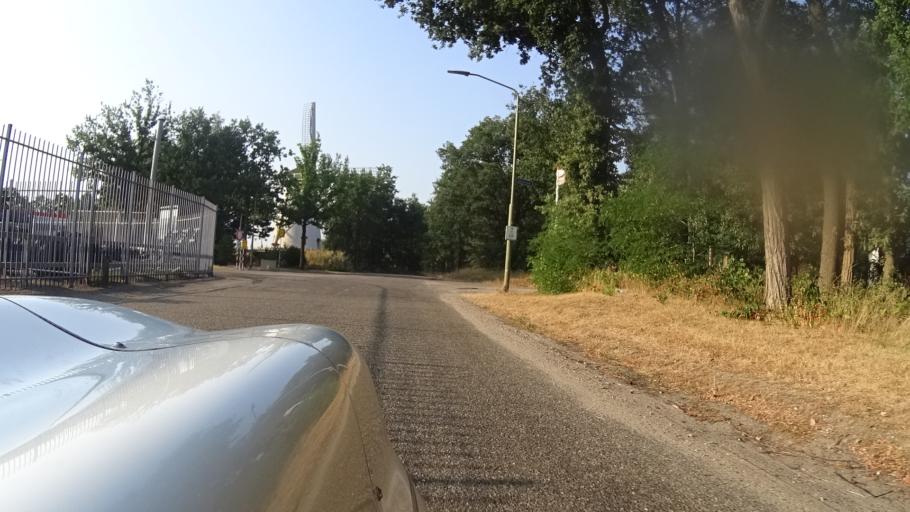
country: NL
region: North Brabant
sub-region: Gemeente Landerd
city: Reek
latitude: 51.7362
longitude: 5.6747
